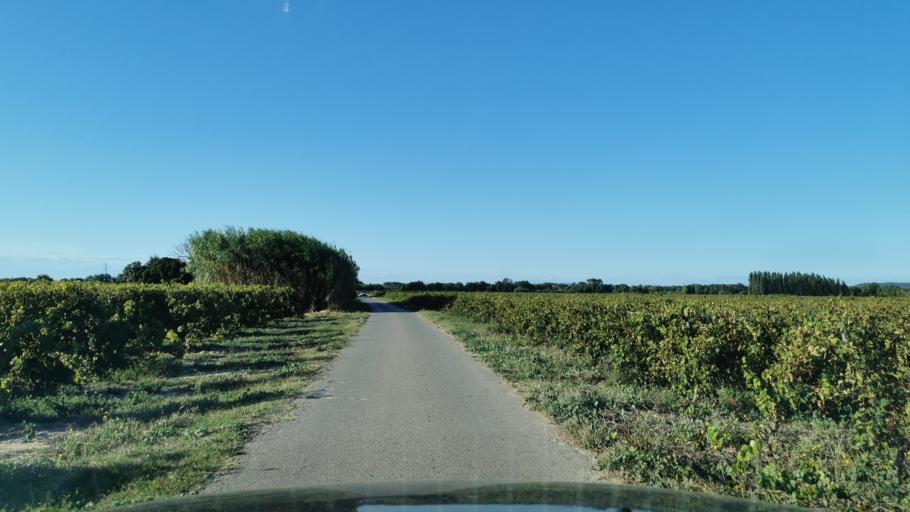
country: FR
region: Languedoc-Roussillon
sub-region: Departement de l'Aude
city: Coursan
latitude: 43.2498
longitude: 3.0188
